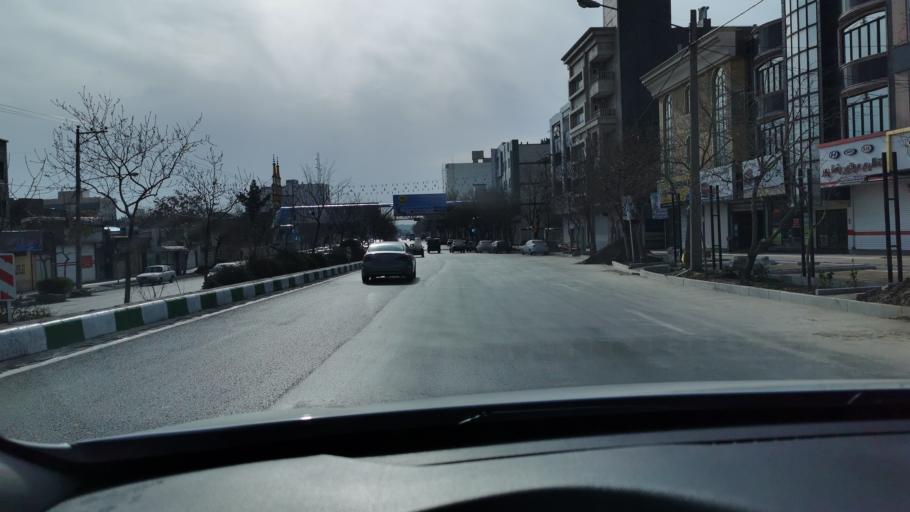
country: IR
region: Razavi Khorasan
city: Mashhad
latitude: 36.2935
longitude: 59.5333
